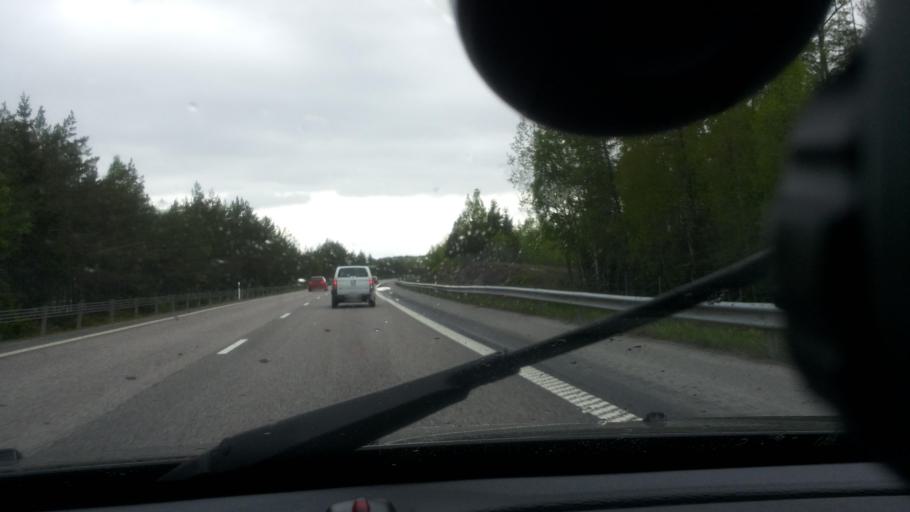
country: SE
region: Uppsala
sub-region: Knivsta Kommun
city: Knivsta
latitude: 59.7025
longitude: 17.8574
